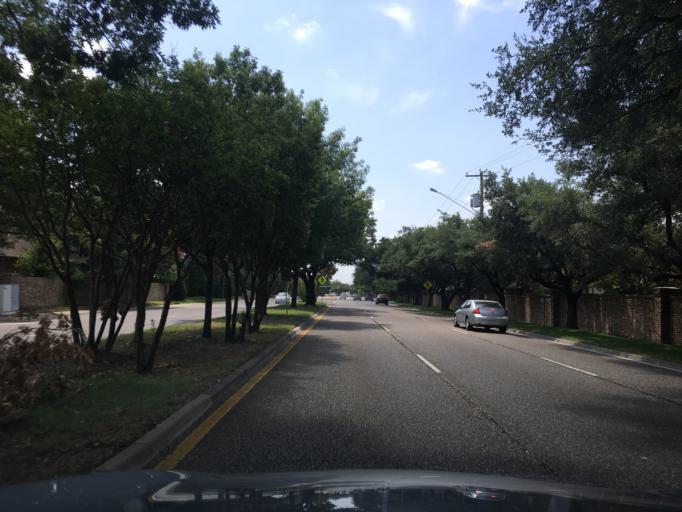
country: US
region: Texas
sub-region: Dallas County
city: Addison
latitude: 32.9204
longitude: -96.8036
